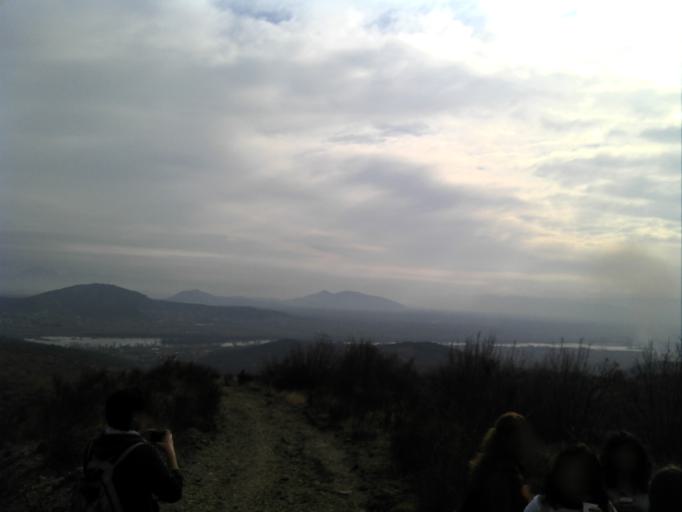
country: AL
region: Shkoder
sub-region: Rrethi i Shkodres
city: Berdica e Madhe
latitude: 42.0357
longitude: 19.4564
